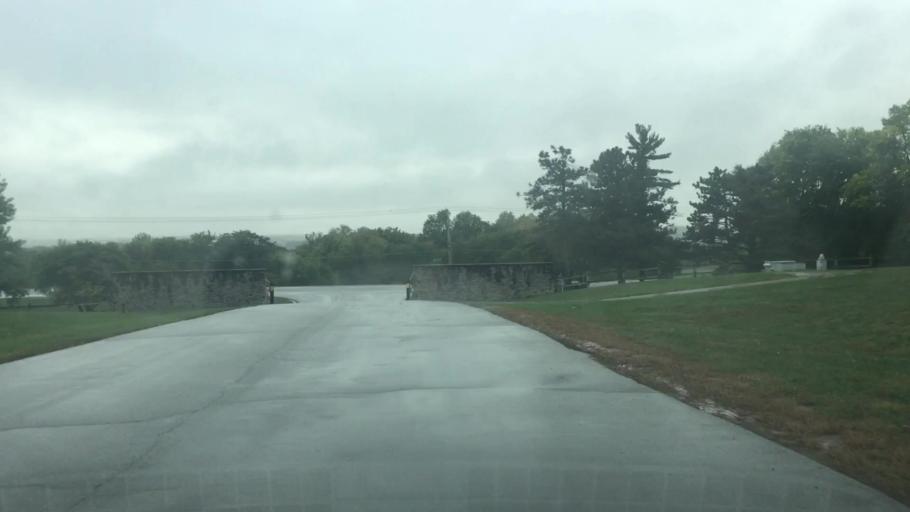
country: US
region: Kansas
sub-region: Johnson County
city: Lenexa
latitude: 38.9718
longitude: -94.8016
